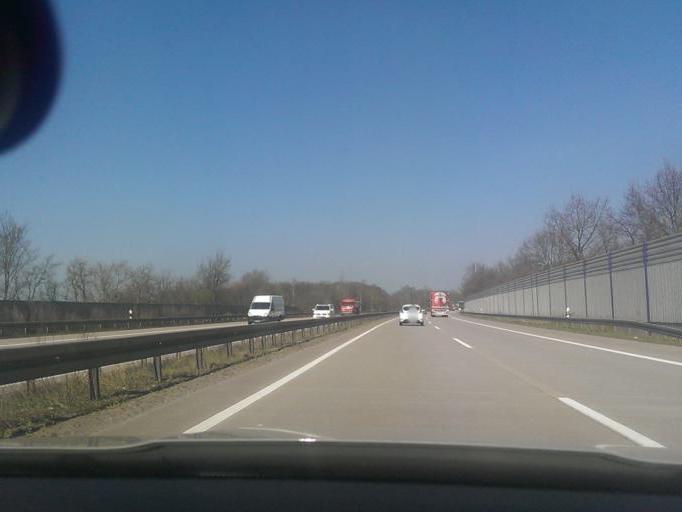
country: DE
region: Lower Saxony
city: Langenhagen
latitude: 52.4776
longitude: 9.7197
